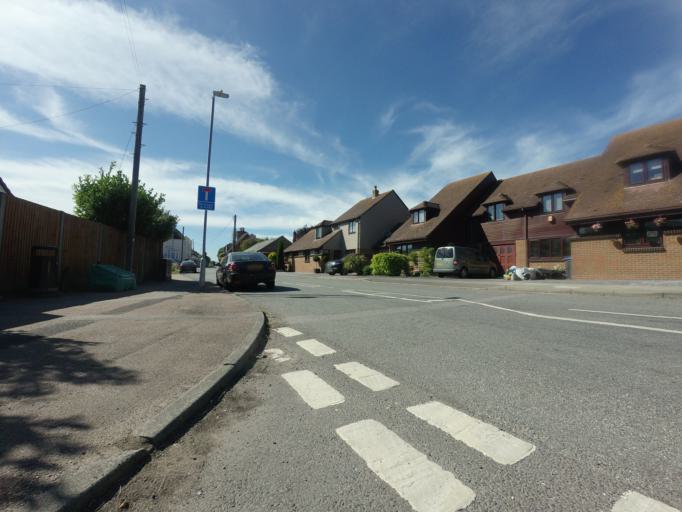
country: GB
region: England
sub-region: Kent
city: Birchington-on-Sea
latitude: 51.3394
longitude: 1.2795
